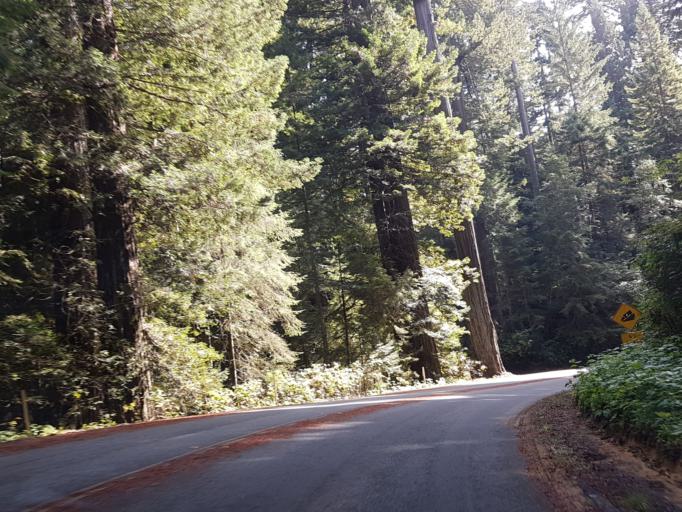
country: US
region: California
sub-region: Del Norte County
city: Bertsch-Oceanview
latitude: 41.4515
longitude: -124.0387
